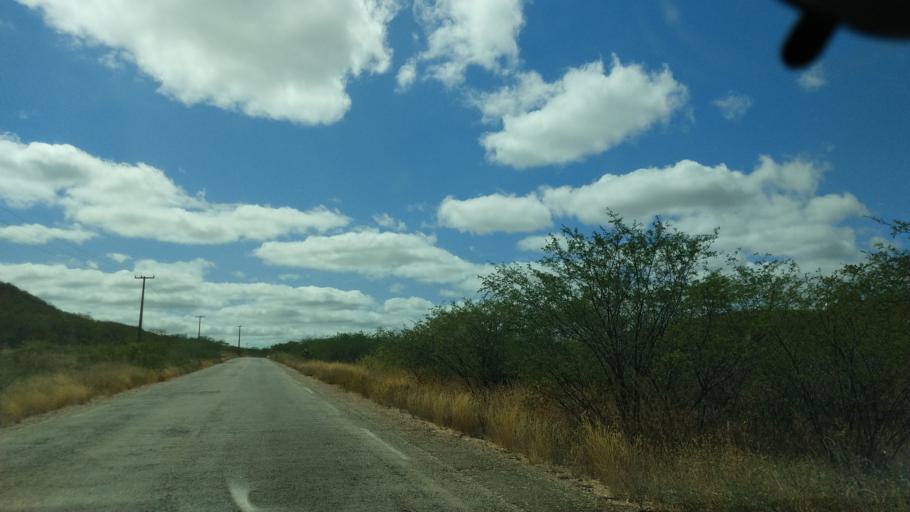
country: BR
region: Rio Grande do Norte
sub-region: Currais Novos
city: Currais Novos
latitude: -6.2628
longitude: -36.5859
